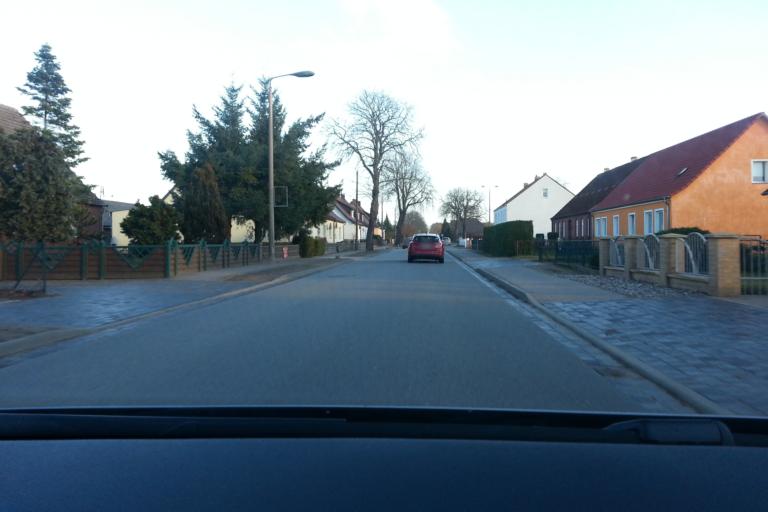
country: DE
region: Mecklenburg-Vorpommern
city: Ferdinandshof
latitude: 53.6633
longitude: 13.8960
